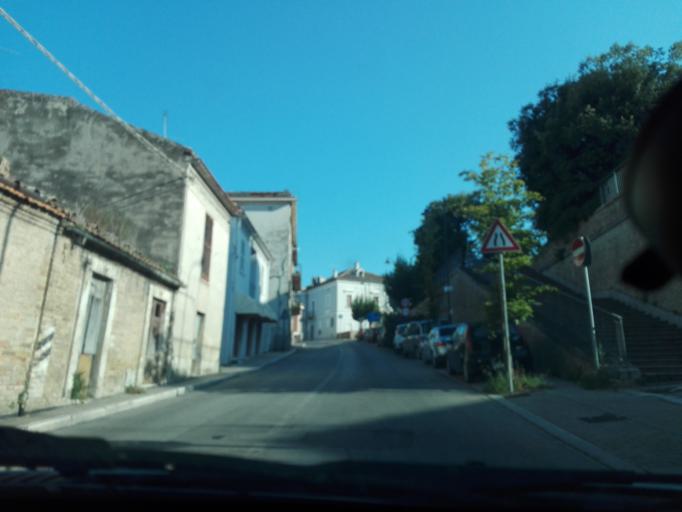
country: IT
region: Abruzzo
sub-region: Provincia di Pescara
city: Cappelle sul Tavo
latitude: 42.4640
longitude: 14.1039
